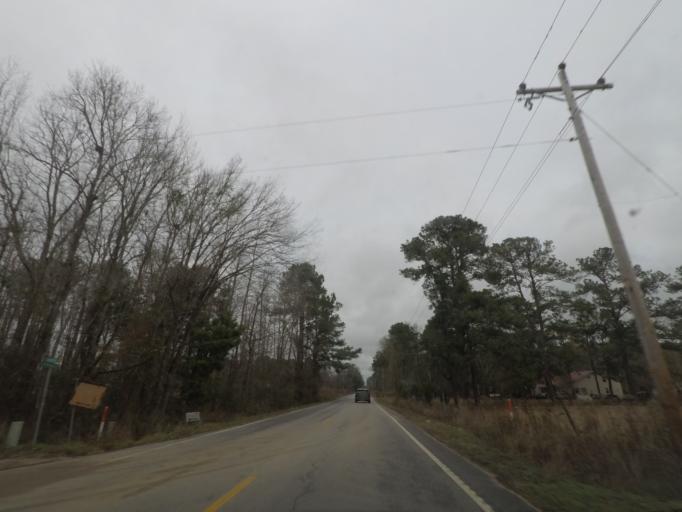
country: US
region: South Carolina
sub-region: Colleton County
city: Walterboro
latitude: 32.8522
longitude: -80.4905
